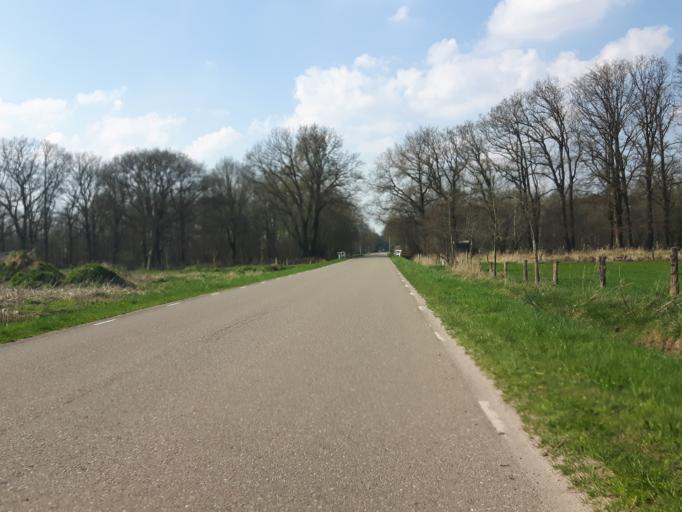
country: NL
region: Overijssel
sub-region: Gemeente Haaksbergen
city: Haaksbergen
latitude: 52.1886
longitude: 6.8039
